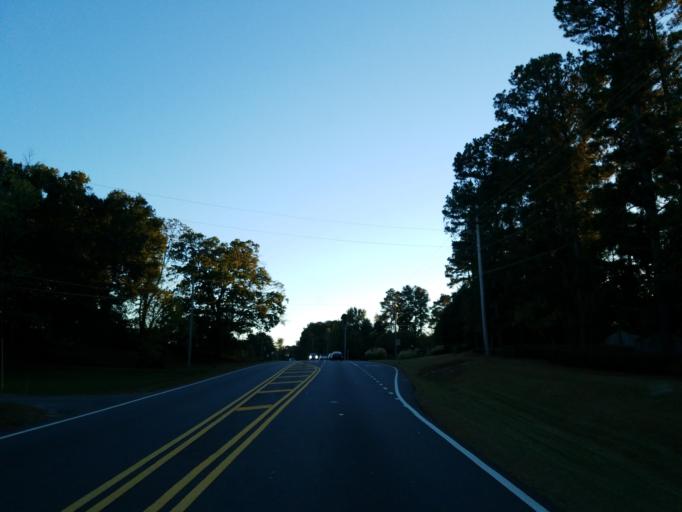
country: US
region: Georgia
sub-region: Forsyth County
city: Cumming
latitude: 34.1781
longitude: -84.1575
